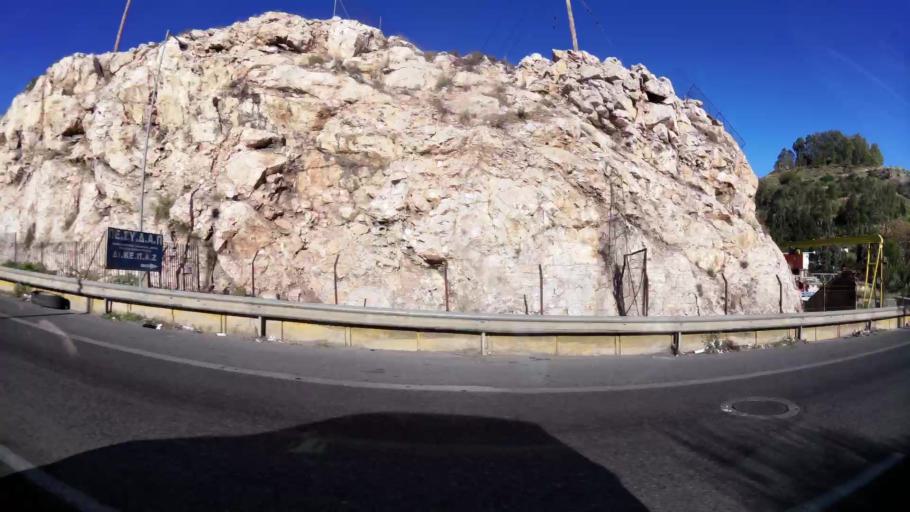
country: GR
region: Attica
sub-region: Nomos Piraios
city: Perama
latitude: 37.9784
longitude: 23.5973
